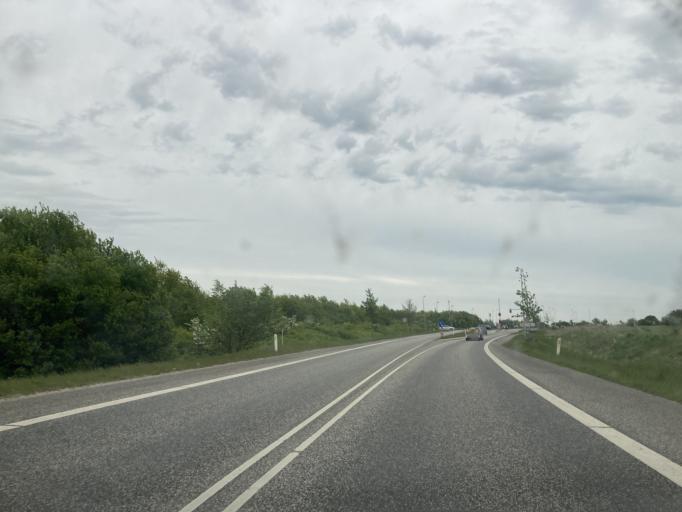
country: DK
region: Zealand
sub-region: Roskilde Kommune
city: Svogerslev
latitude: 55.6290
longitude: 12.0371
